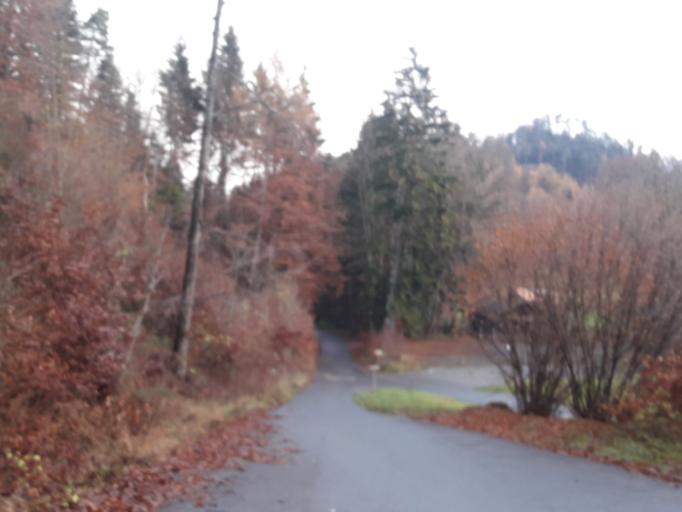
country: CH
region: Bern
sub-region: Interlaken-Oberhasli District
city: Wilderswil
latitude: 46.6718
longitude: 7.8529
